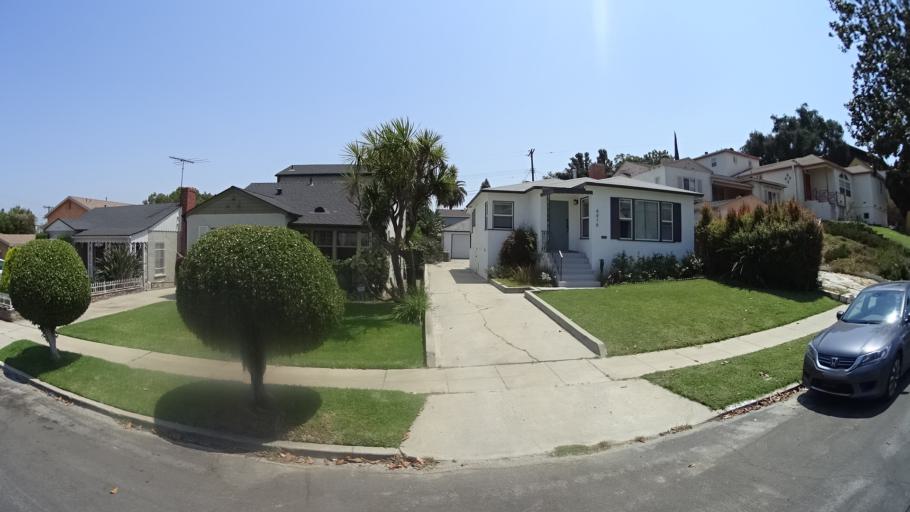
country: US
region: California
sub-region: Los Angeles County
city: View Park-Windsor Hills
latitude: 33.9861
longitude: -118.3525
